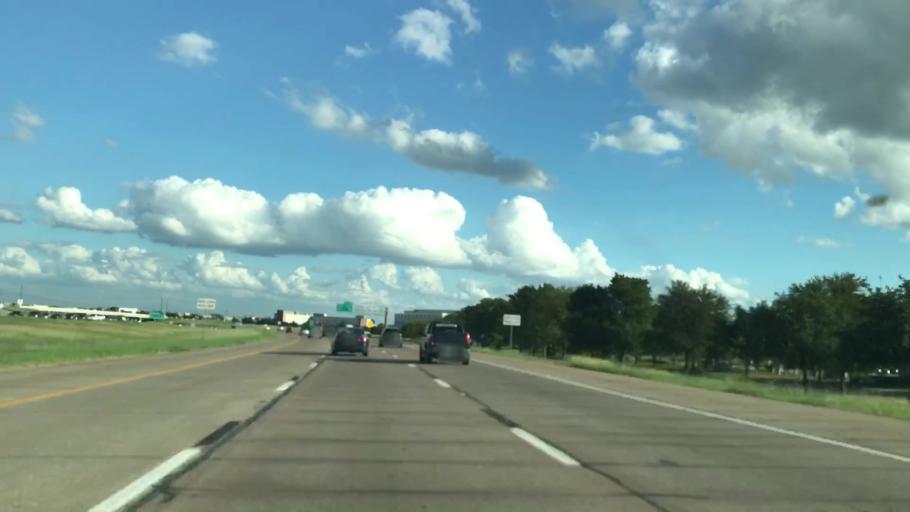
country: US
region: Texas
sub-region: Dallas County
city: Coppell
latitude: 32.9274
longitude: -97.0020
